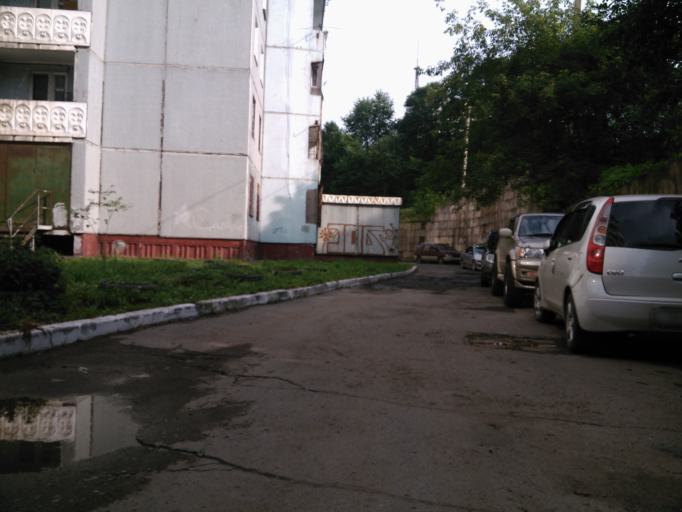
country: RU
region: Primorskiy
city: Vladivostok
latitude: 43.0941
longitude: 131.9612
